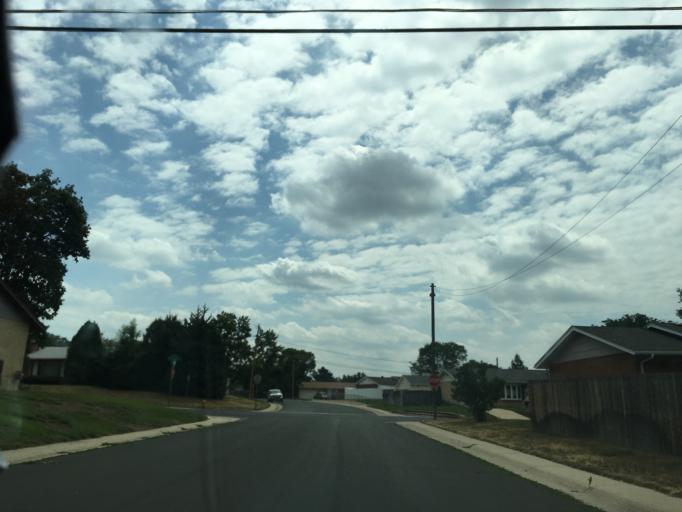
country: US
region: Colorado
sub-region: Arapahoe County
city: Sheridan
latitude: 39.6640
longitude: -105.0407
